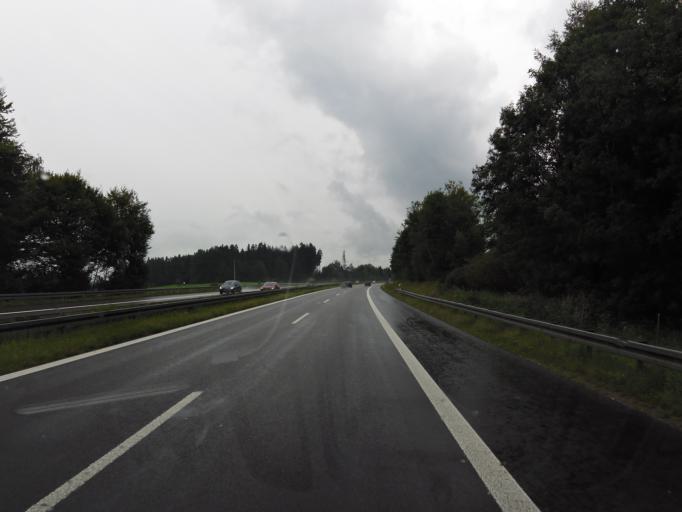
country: DE
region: Baden-Wuerttemberg
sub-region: Tuebingen Region
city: Neukirch
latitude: 47.6335
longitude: 9.7407
